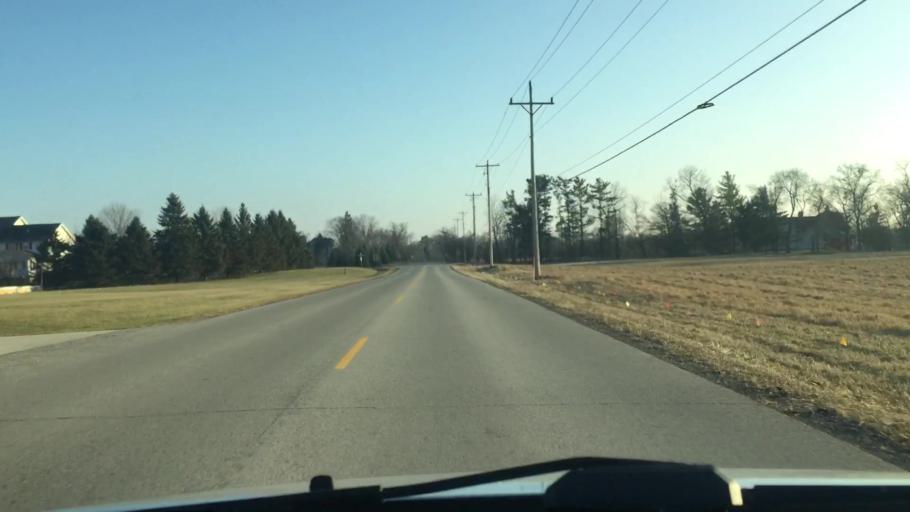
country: US
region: Wisconsin
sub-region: Waukesha County
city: Dousman
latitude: 43.0363
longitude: -88.4826
